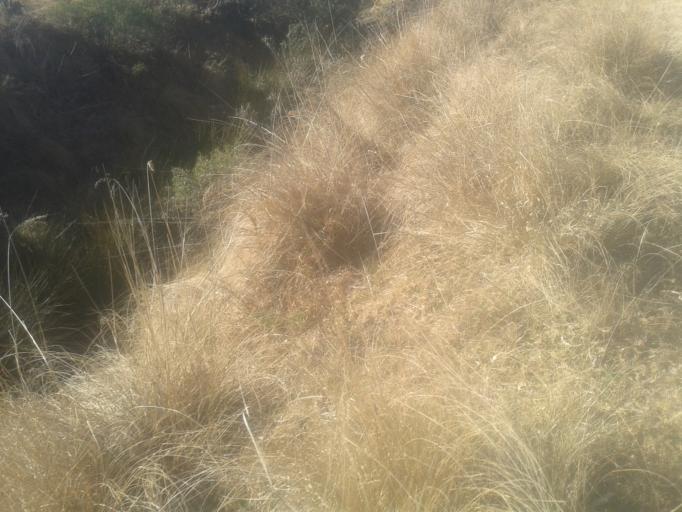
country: MX
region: Mexico
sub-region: Acambay de Ruiz Castaneda
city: La Caridad
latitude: 19.9013
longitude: -99.8544
